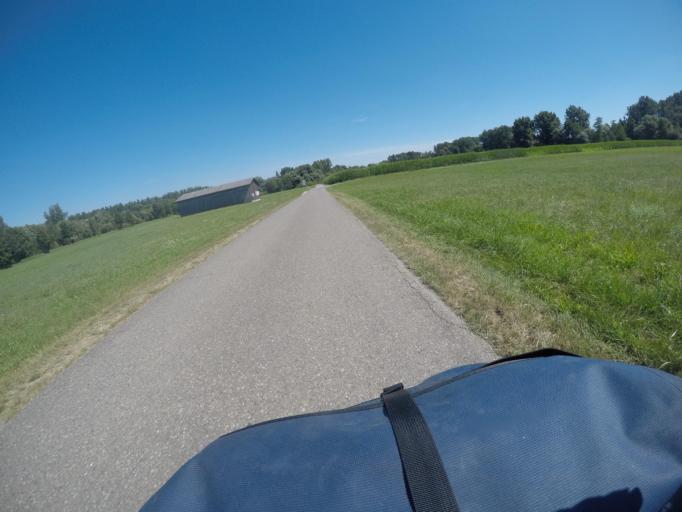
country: DE
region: Baden-Wuerttemberg
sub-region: Tuebingen Region
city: Neufra
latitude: 48.1310
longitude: 9.4633
